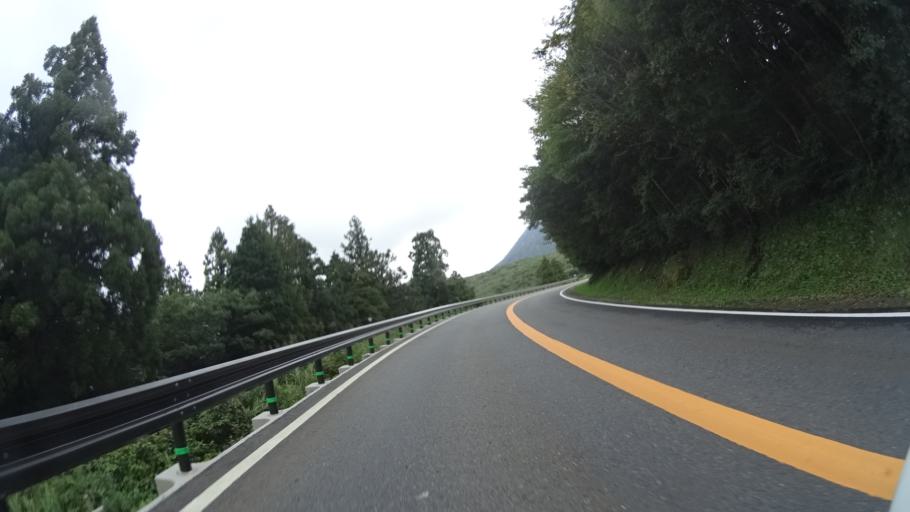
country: JP
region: Oita
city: Tsukawaki
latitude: 33.1020
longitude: 131.2241
